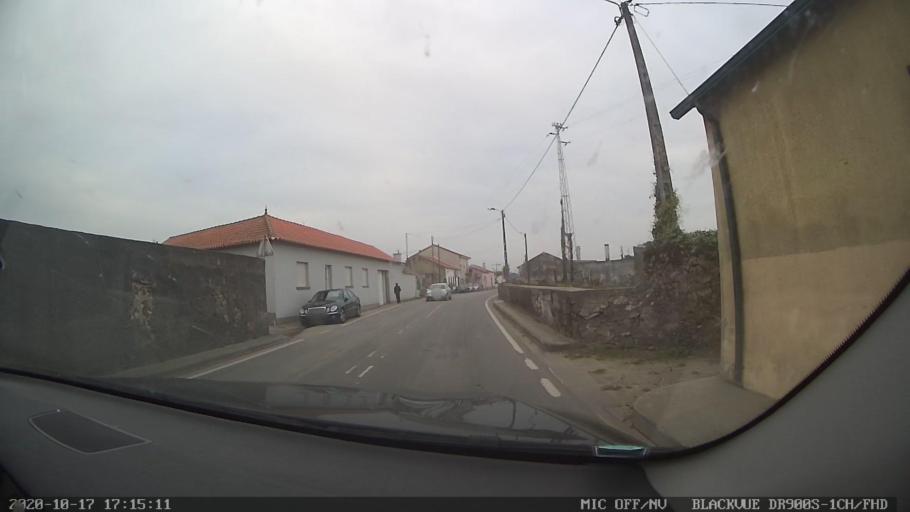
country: PT
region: Braga
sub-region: Esposende
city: Apulia
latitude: 41.4930
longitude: -8.7552
